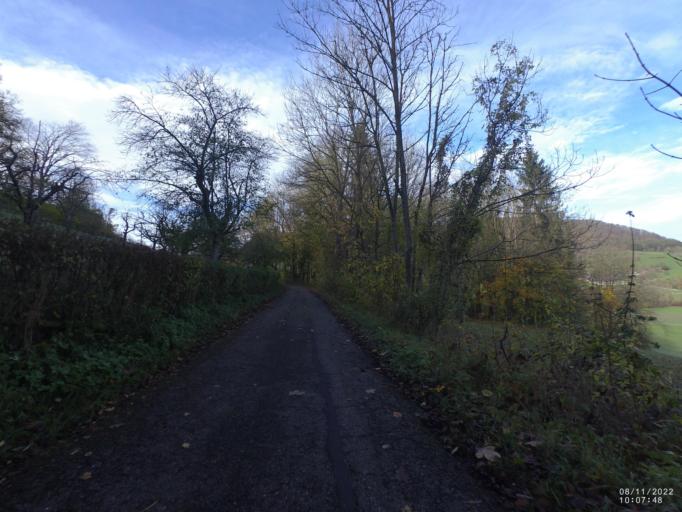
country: DE
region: Baden-Wuerttemberg
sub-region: Regierungsbezirk Stuttgart
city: Deggingen
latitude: 48.6047
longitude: 9.7378
